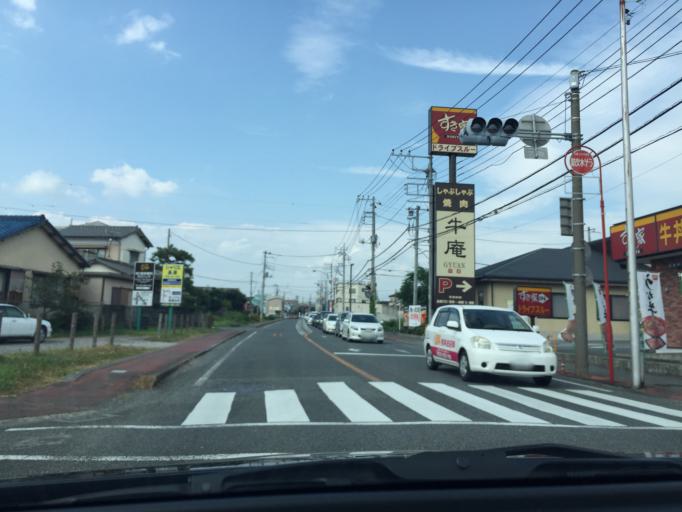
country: JP
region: Shizuoka
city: Mishima
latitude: 35.1258
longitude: 138.8984
